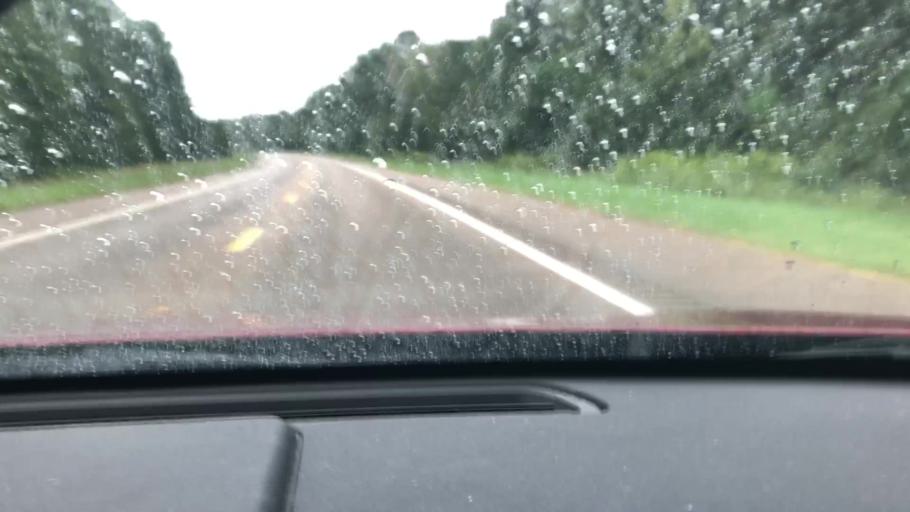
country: US
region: Arkansas
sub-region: Columbia County
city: Magnolia
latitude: 33.2988
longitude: -93.2638
